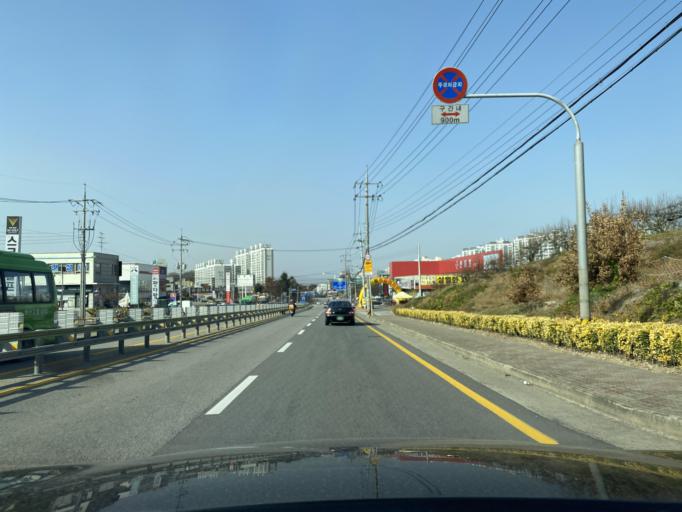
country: KR
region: Chungcheongnam-do
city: Yesan
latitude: 36.6917
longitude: 126.8388
